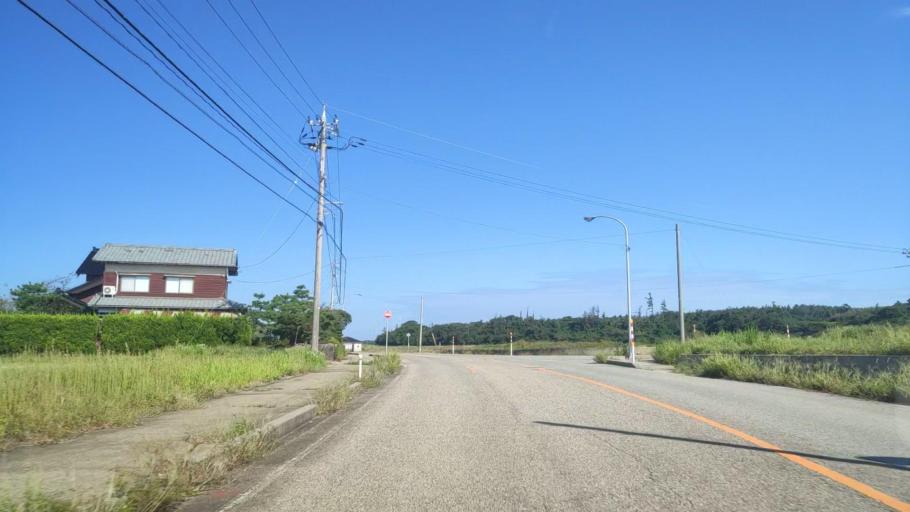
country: JP
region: Ishikawa
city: Hakui
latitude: 37.0342
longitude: 136.7469
